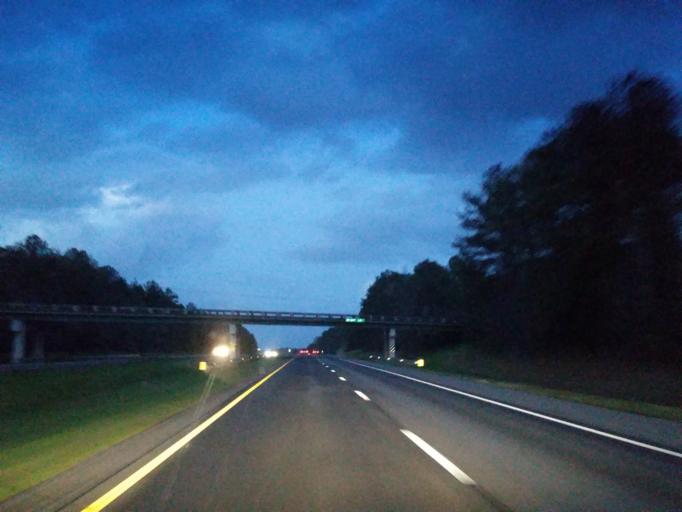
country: US
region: Alabama
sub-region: Sumter County
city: Livingston
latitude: 32.5949
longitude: -88.2244
